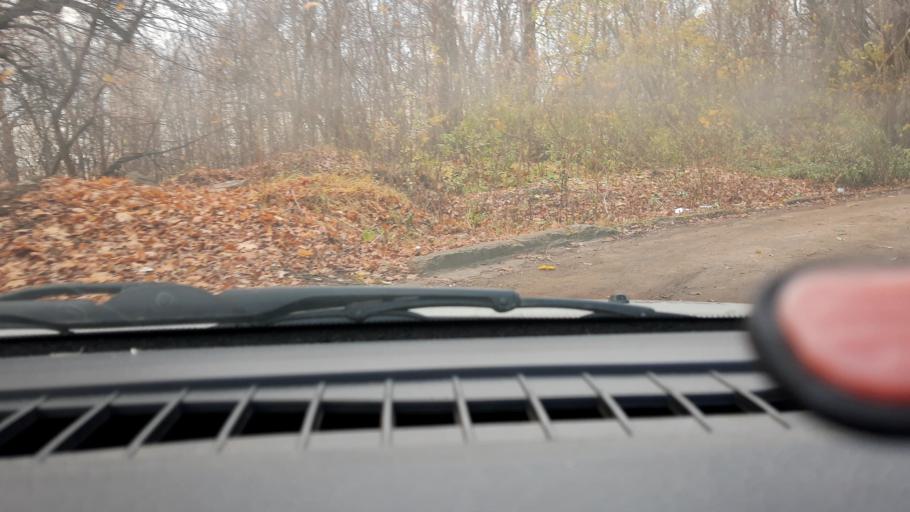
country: RU
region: Nizjnij Novgorod
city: Nizhniy Novgorod
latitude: 56.2968
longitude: 43.9747
